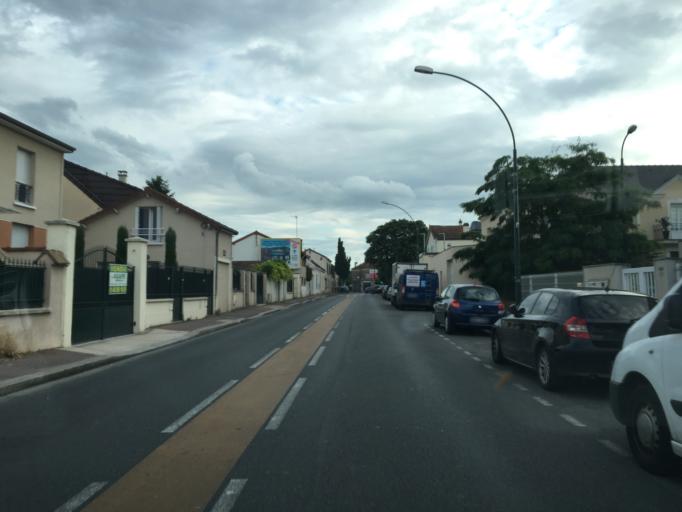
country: FR
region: Ile-de-France
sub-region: Departement du Val-de-Marne
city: Saint-Maur-des-Fosses
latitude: 48.7905
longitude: 2.4961
